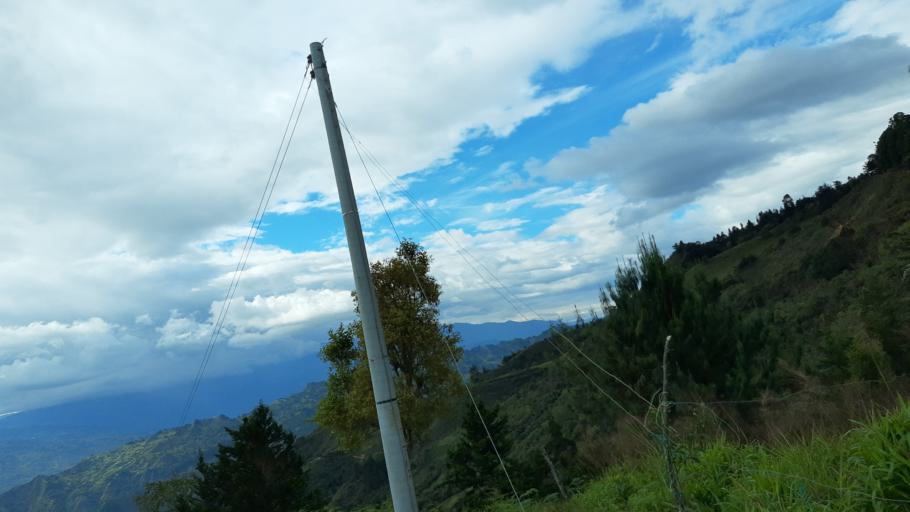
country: CO
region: Boyaca
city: Garagoa
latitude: 4.9987
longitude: -73.3377
